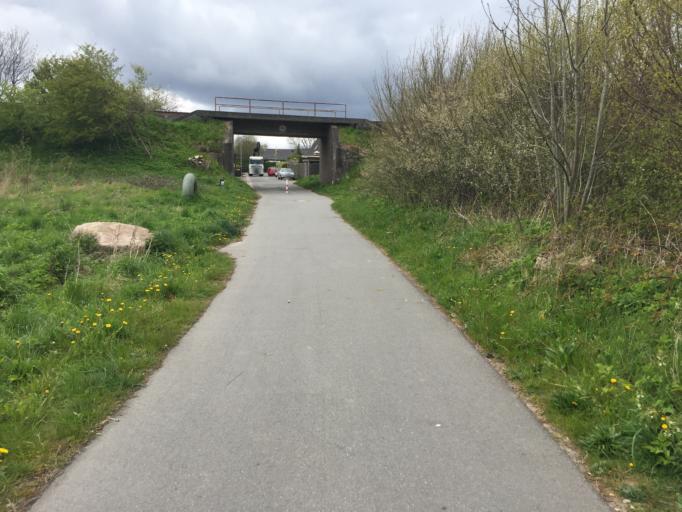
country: DE
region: Schleswig-Holstein
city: Tastrup
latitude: 54.7717
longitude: 9.4675
